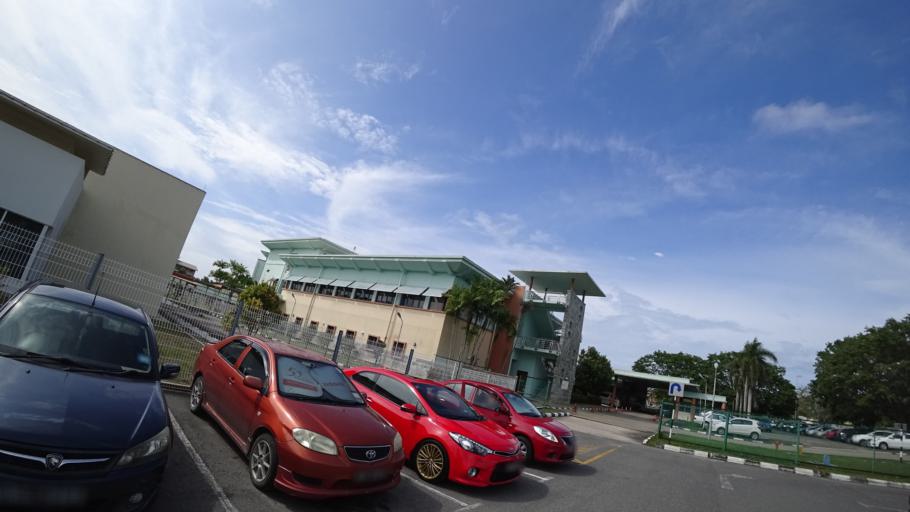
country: BN
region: Tutong
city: Tutong
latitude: 4.8163
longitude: 114.6637
